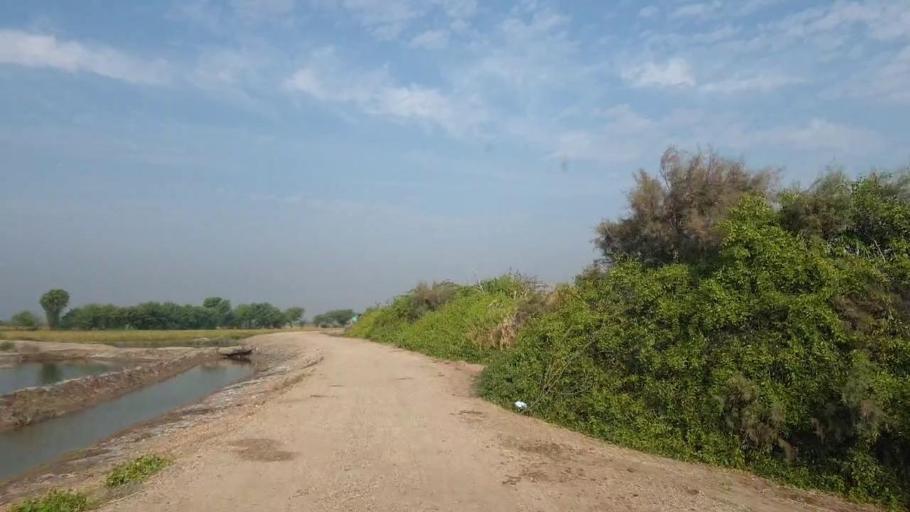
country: PK
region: Sindh
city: Tando Bago
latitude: 24.8560
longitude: 68.9876
